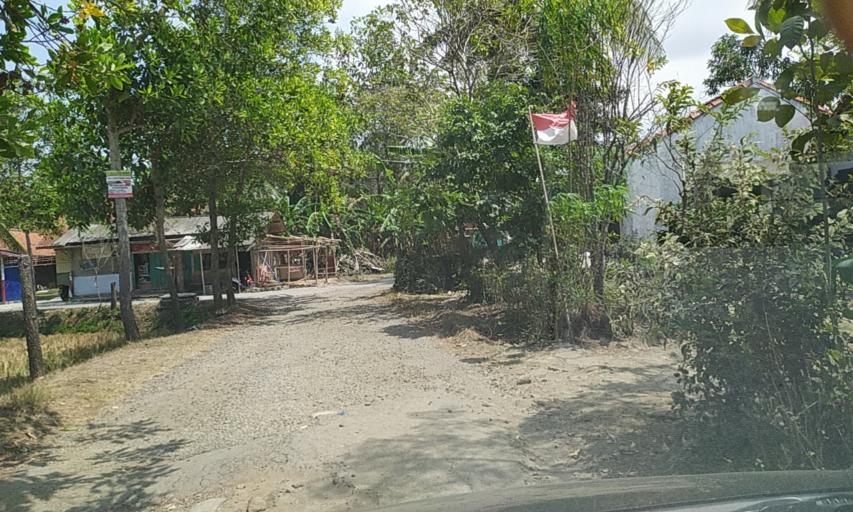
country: ID
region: Central Java
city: Sawoan
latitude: -7.6379
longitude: 109.0646
